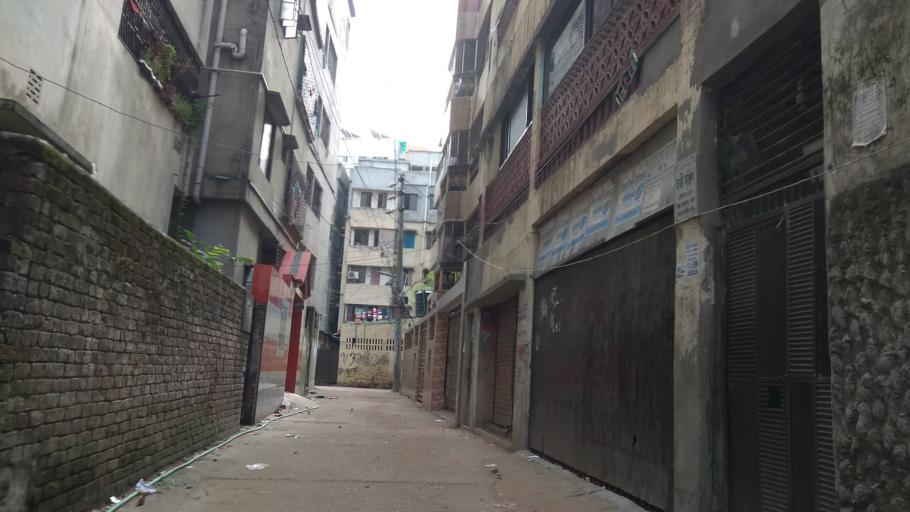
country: BD
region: Dhaka
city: Azimpur
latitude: 23.7931
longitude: 90.3812
